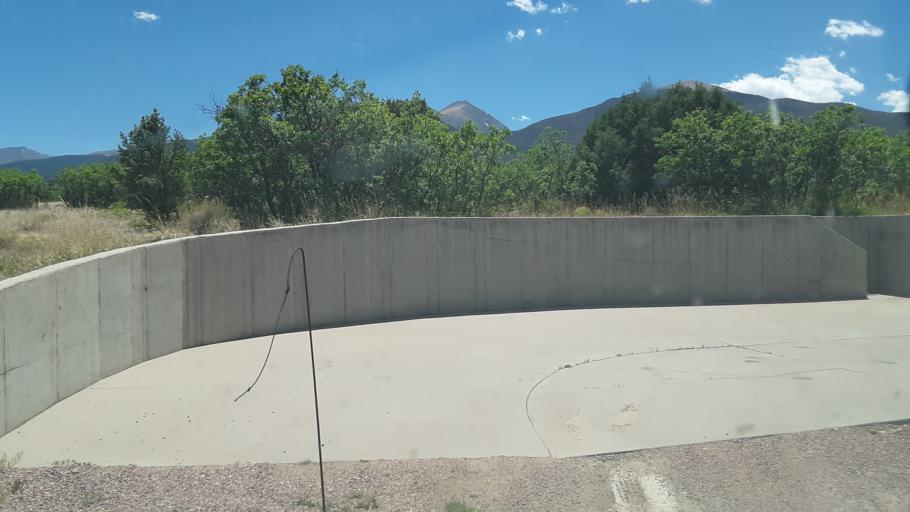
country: US
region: Colorado
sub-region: Custer County
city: Westcliffe
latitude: 38.3002
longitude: -105.6787
